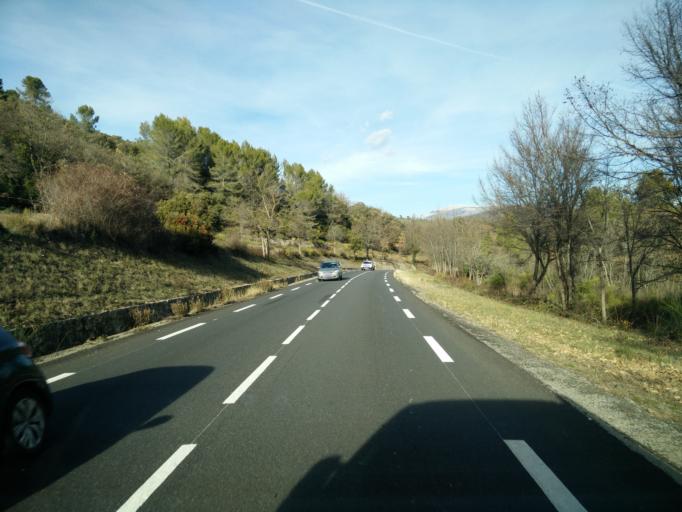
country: FR
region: Provence-Alpes-Cote d'Azur
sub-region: Departement du Var
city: Montauroux
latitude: 43.6045
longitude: 6.8071
